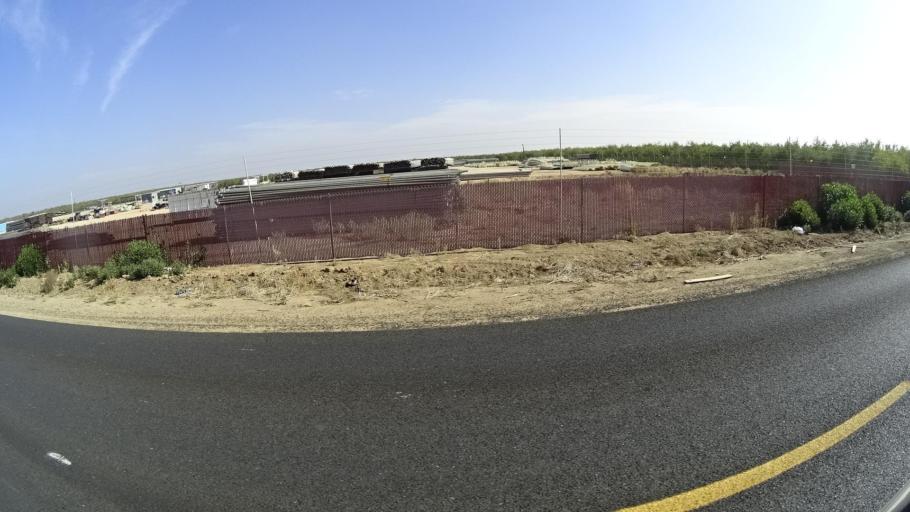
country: US
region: California
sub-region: Kern County
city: Shafter
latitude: 35.5182
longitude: -119.1519
